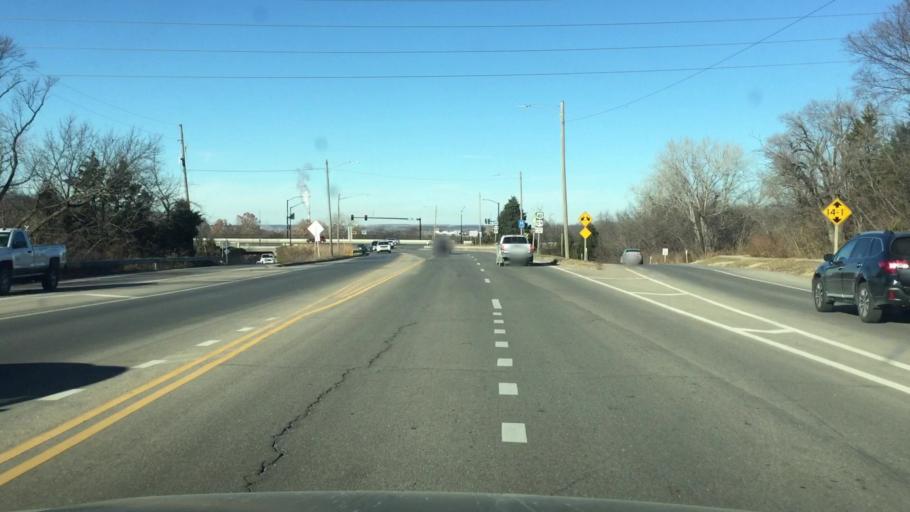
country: US
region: Kansas
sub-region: Douglas County
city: Lawrence
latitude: 38.9710
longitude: -95.2604
